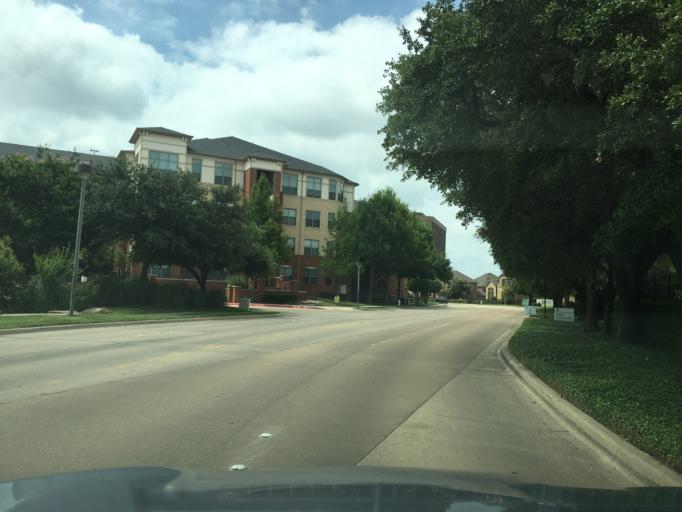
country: US
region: Texas
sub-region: Dallas County
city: Addison
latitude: 32.9361
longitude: -96.8405
